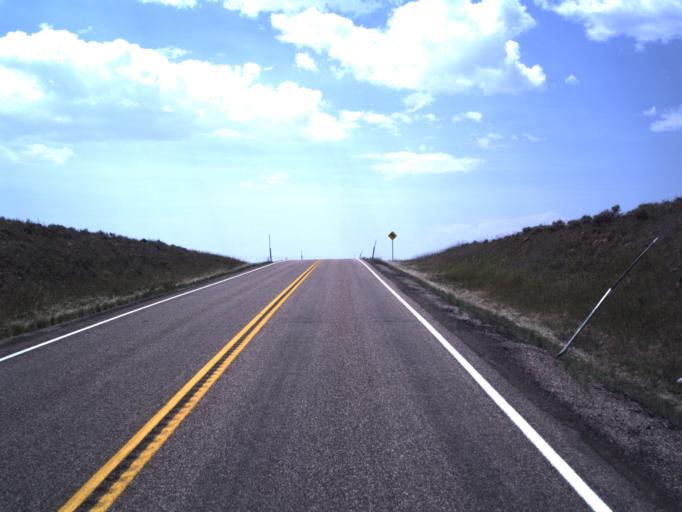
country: US
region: Utah
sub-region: Uintah County
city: Maeser
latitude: 40.6935
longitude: -109.4939
